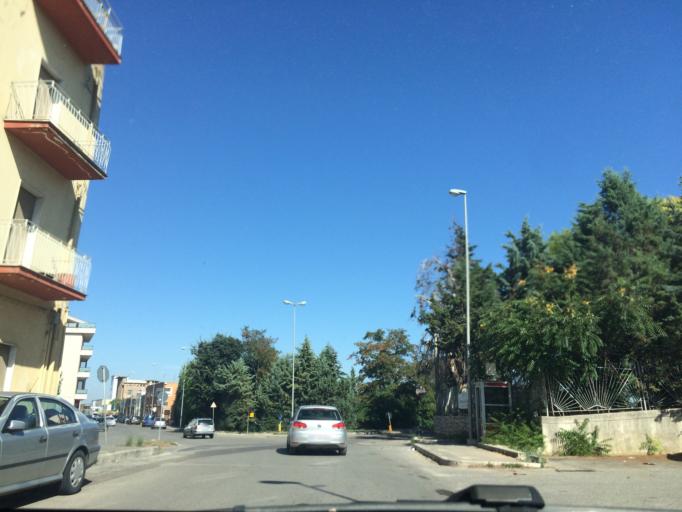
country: IT
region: Basilicate
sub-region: Provincia di Matera
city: Matera
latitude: 40.6741
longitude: 16.6061
